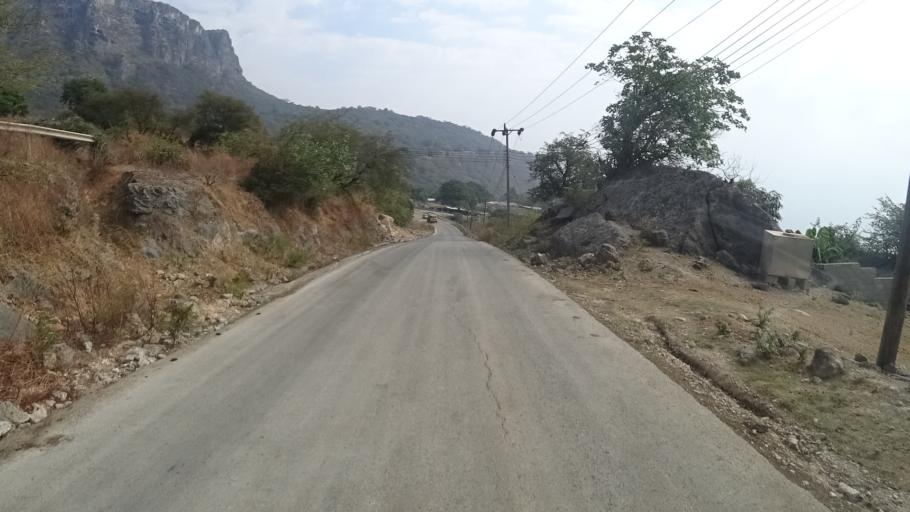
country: YE
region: Al Mahrah
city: Hawf
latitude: 16.7080
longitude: 53.2259
